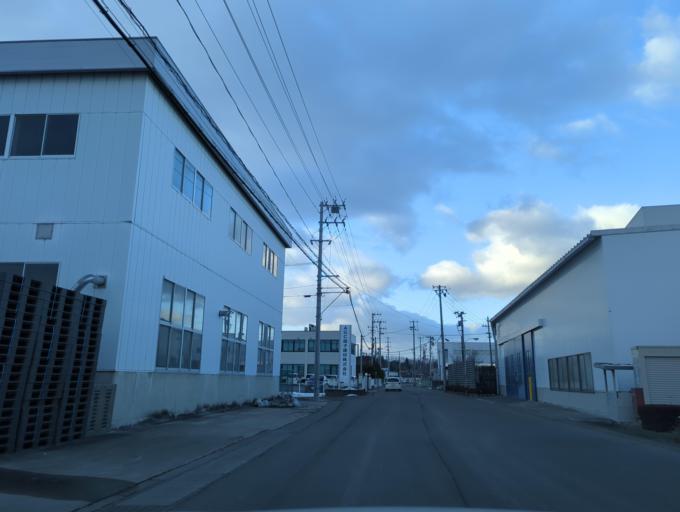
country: JP
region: Fukushima
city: Koriyama
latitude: 37.4247
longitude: 140.4042
